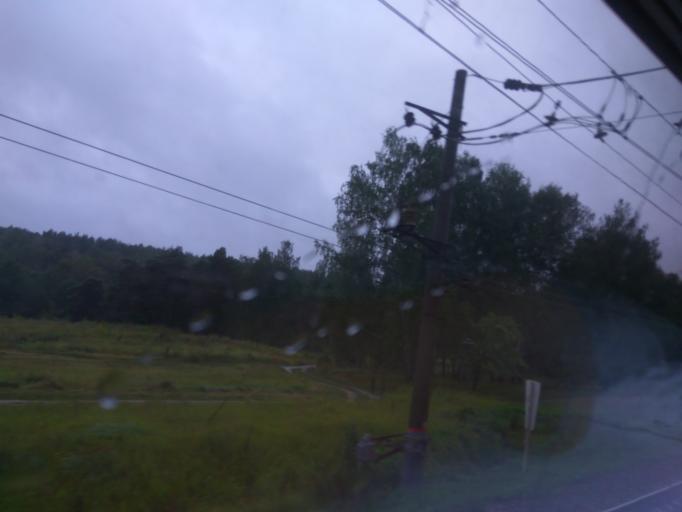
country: RU
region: Moskovskaya
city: Stupino
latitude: 54.8774
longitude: 38.1119
